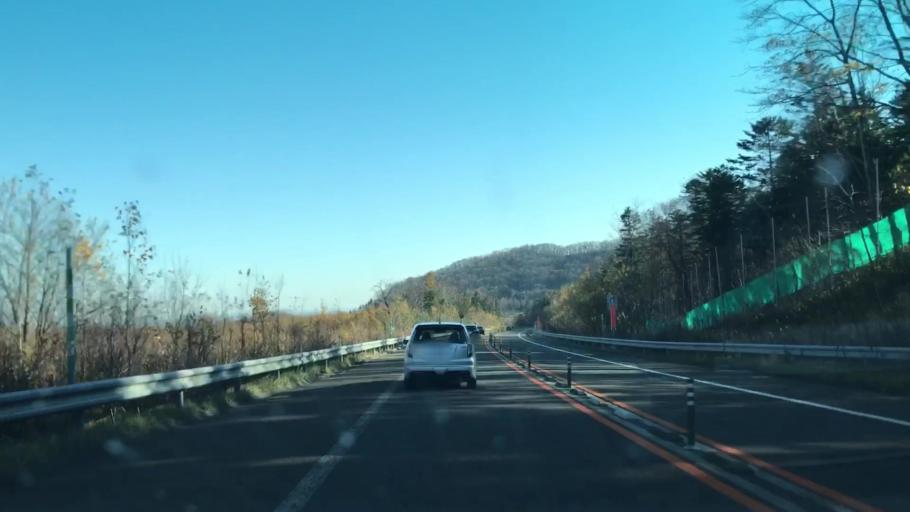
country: JP
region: Hokkaido
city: Otofuke
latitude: 43.0152
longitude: 142.8303
